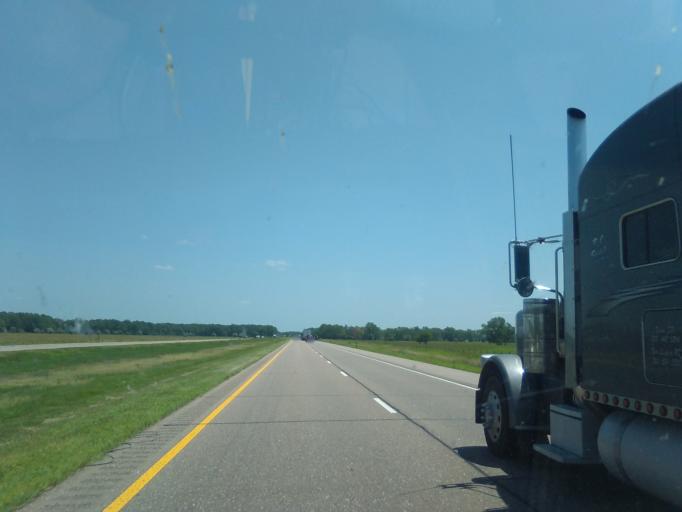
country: US
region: Nebraska
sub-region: Dawson County
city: Gothenburg
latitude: 40.8947
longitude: -100.1173
